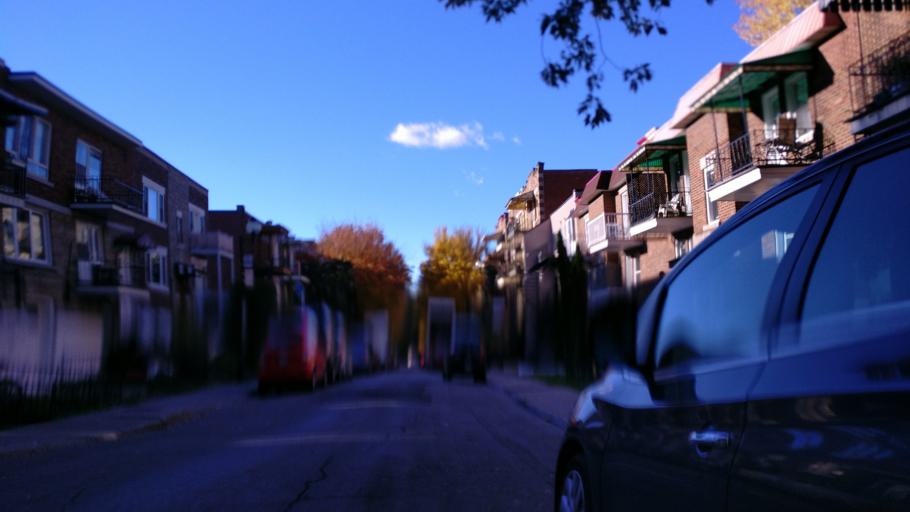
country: CA
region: Quebec
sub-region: Montreal
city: Montreal
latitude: 45.5336
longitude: -73.5634
